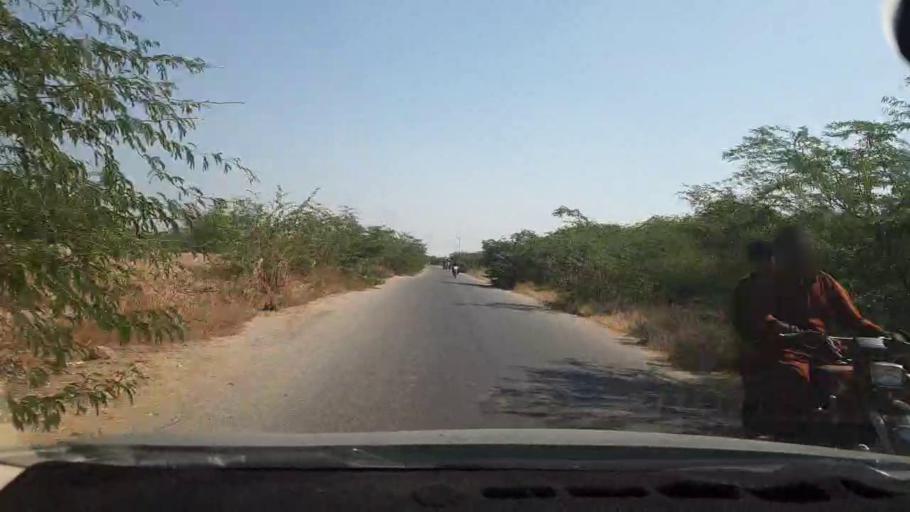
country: PK
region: Sindh
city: Malir Cantonment
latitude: 25.1410
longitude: 67.2014
